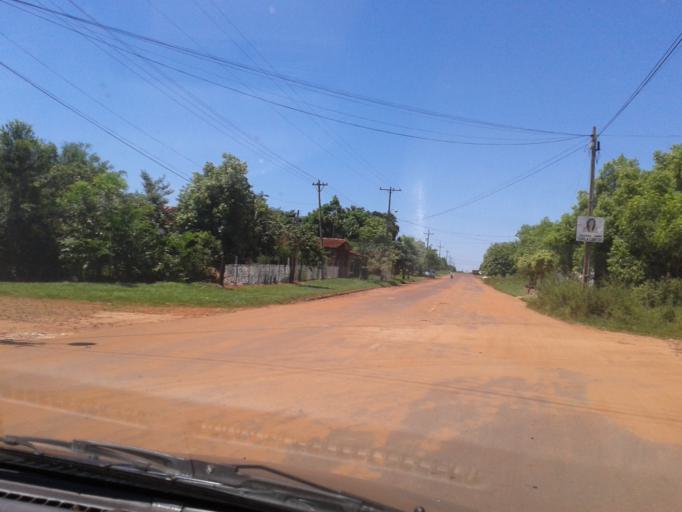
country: PY
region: Misiones
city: Santa Maria
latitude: -26.8984
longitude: -57.0278
